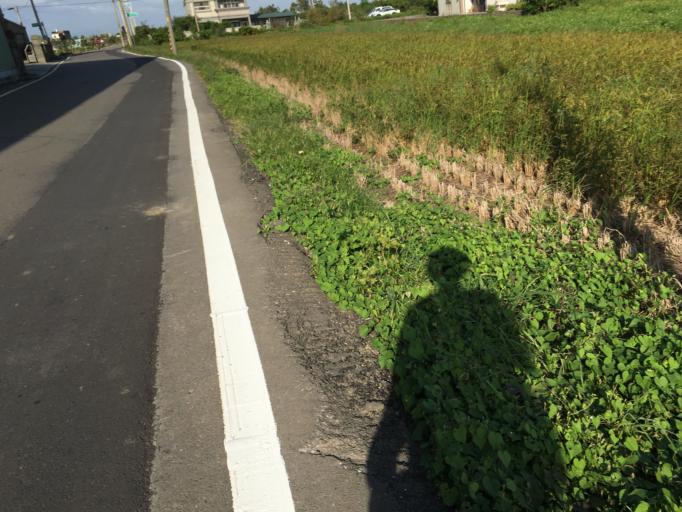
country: TW
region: Taiwan
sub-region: Hsinchu
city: Zhubei
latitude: 24.9282
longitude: 120.9859
